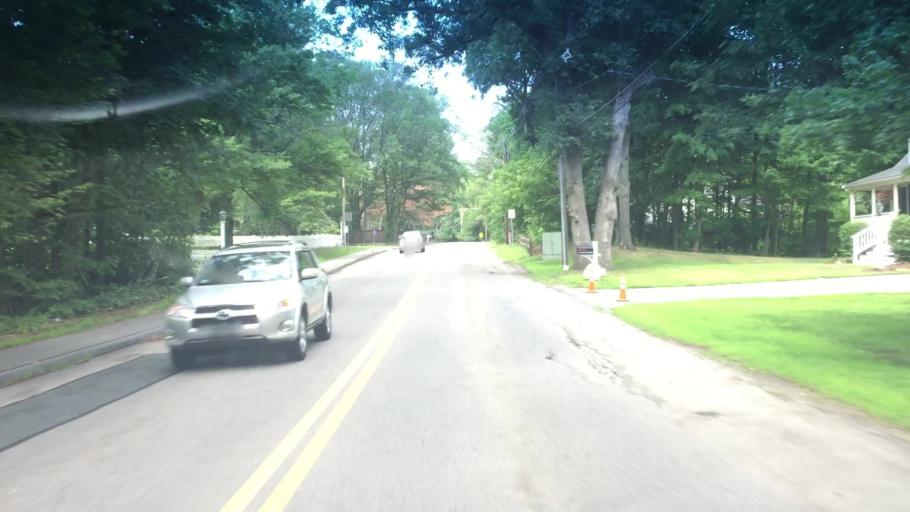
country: US
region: Massachusetts
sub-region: Norfolk County
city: Franklin
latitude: 42.0954
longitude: -71.3960
